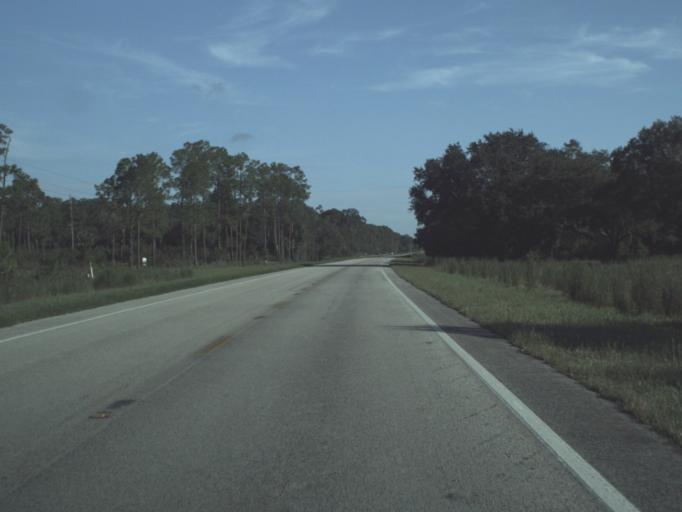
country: US
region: Florida
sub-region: Pasco County
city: Zephyrhills North
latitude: 28.2986
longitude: -82.0557
